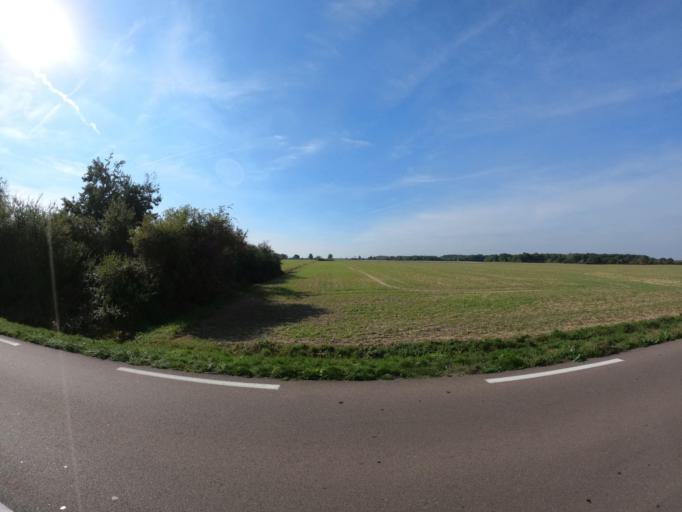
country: FR
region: Bourgogne
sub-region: Departement de Saone-et-Loire
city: Saint-Martin-en-Bresse
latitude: 46.7451
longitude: 5.0613
